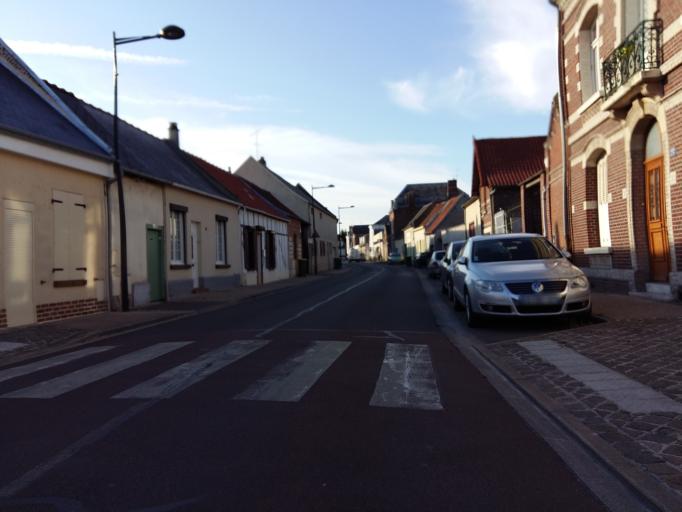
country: FR
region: Picardie
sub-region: Departement de la Somme
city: Camon
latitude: 49.8885
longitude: 2.3426
